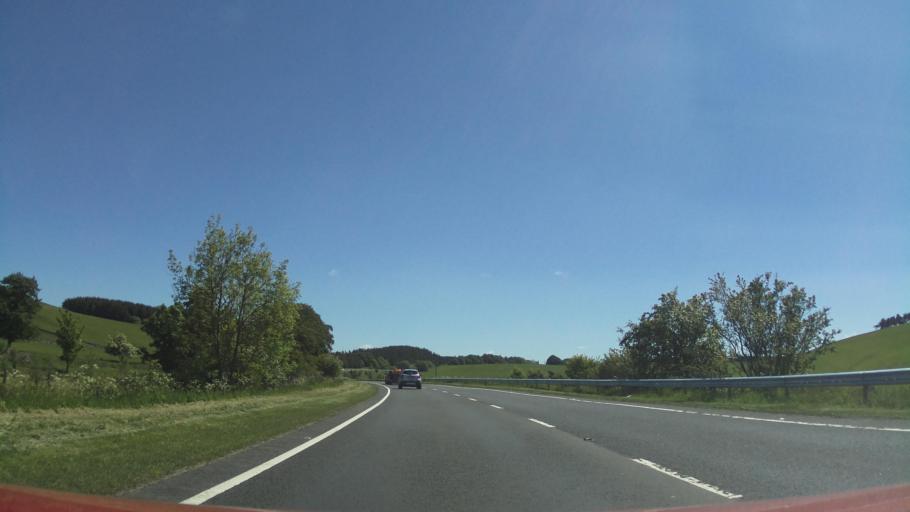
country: GB
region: Scotland
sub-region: The Scottish Borders
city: Selkirk
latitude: 55.4833
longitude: -2.8314
